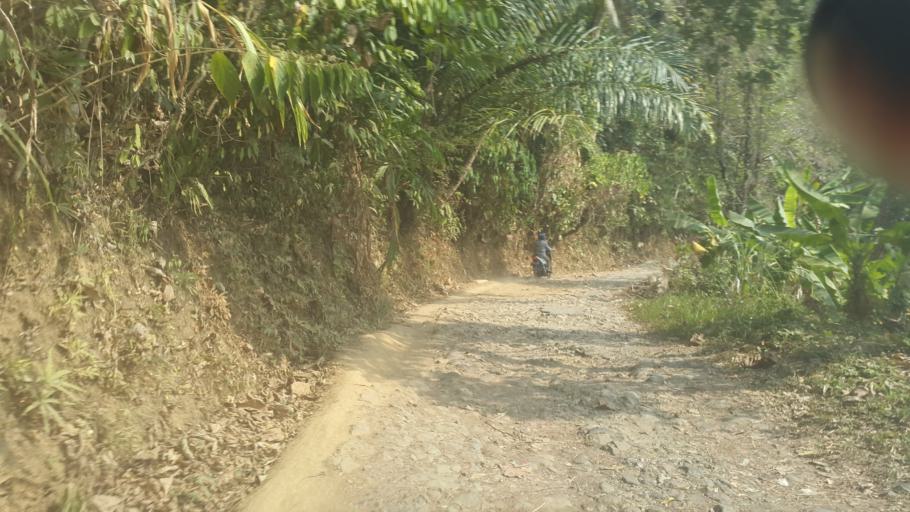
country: ID
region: West Java
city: Tugu
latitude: -6.9427
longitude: 106.4451
